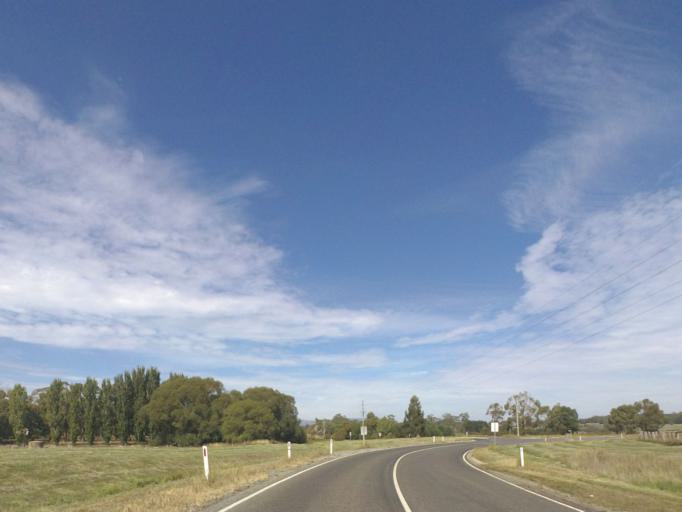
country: AU
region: Victoria
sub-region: Mount Alexander
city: Castlemaine
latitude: -37.2634
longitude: 144.4860
